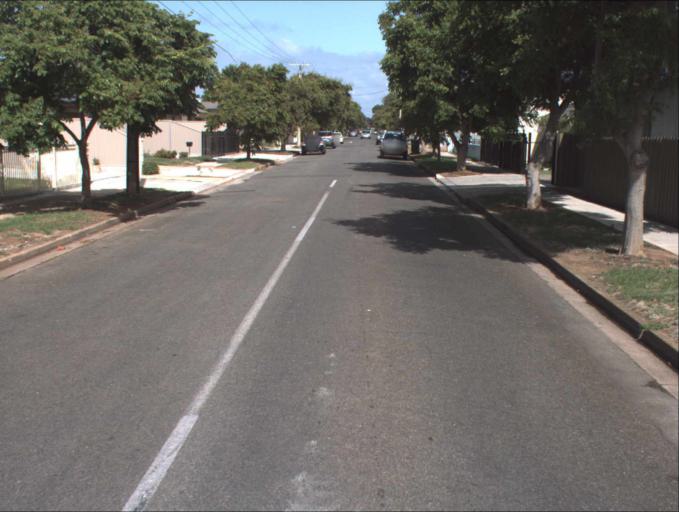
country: AU
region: South Australia
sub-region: Charles Sturt
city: Woodville North
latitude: -34.8712
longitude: 138.5543
